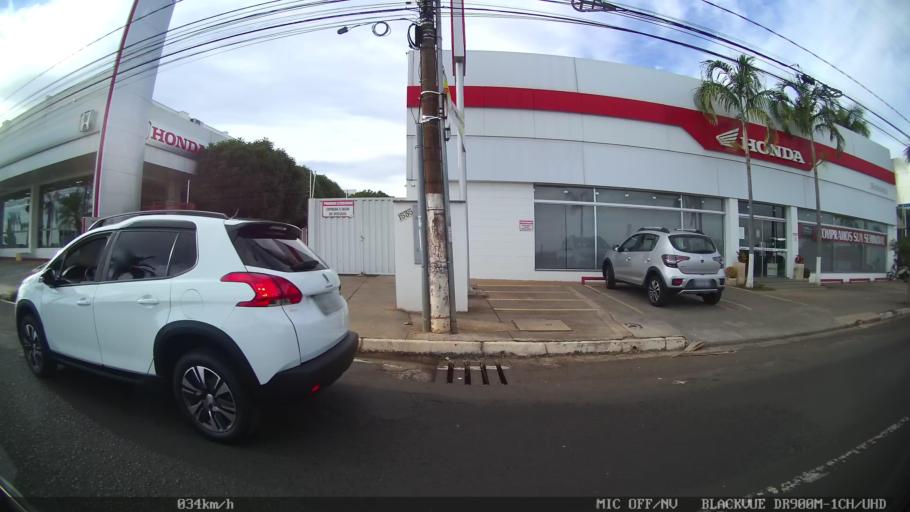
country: BR
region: Sao Paulo
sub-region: Catanduva
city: Catanduva
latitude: -21.1506
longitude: -48.9887
